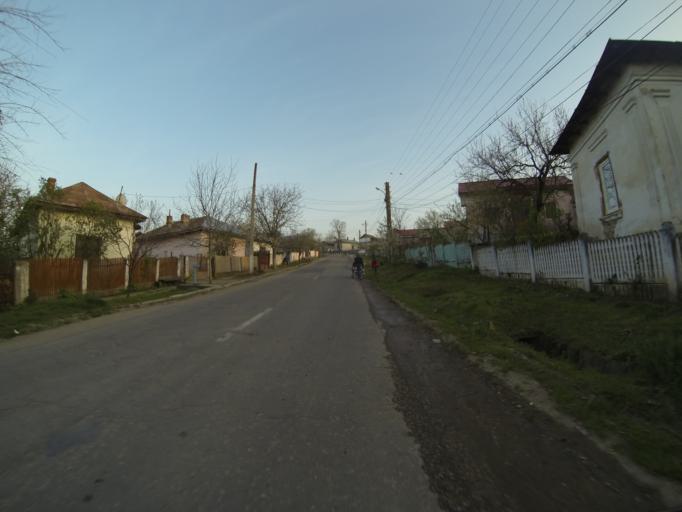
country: RO
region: Dolj
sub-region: Comuna Dranicu
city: Dranic
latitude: 44.0541
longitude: 23.8459
